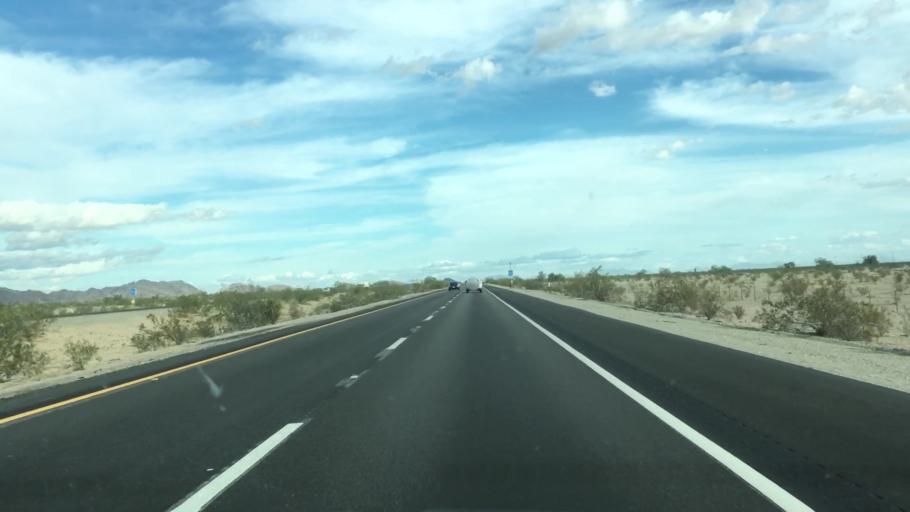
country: US
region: California
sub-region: Riverside County
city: Mesa Verde
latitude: 33.6093
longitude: -114.8517
